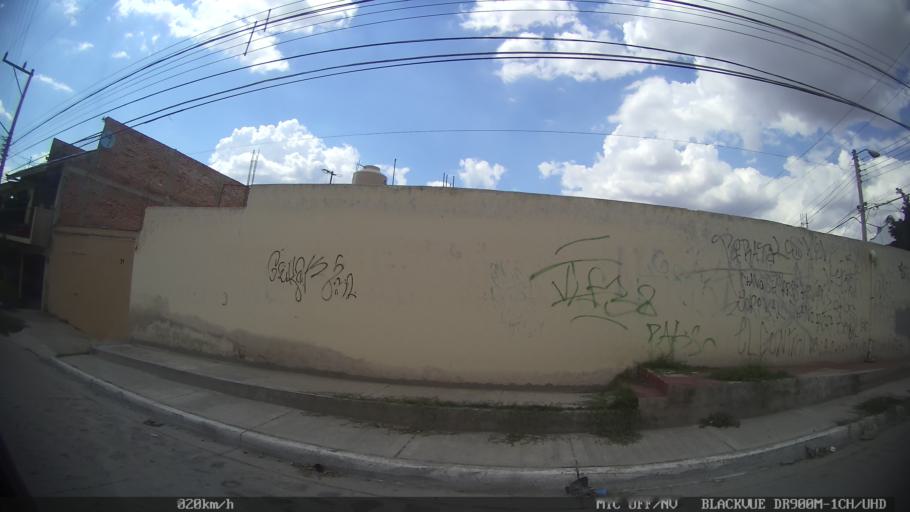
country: MX
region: Jalisco
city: Tlaquepaque
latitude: 20.6790
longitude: -103.2645
